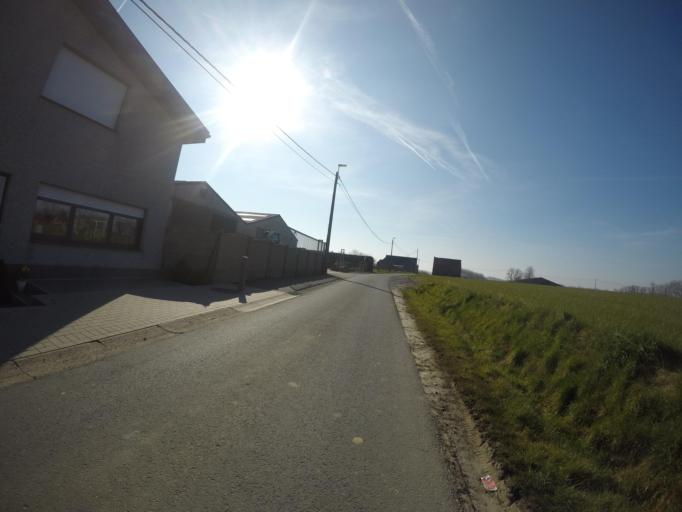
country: BE
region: Flanders
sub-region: Provincie Oost-Vlaanderen
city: Sint-Maria-Lierde
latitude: 50.8024
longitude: 3.7962
